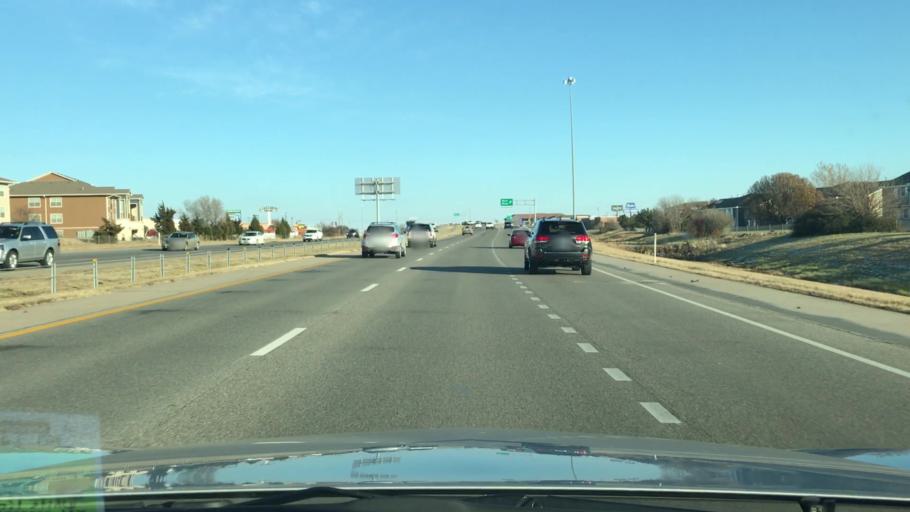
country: US
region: Kansas
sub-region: Sedgwick County
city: Bellaire
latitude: 37.7451
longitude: -97.2511
